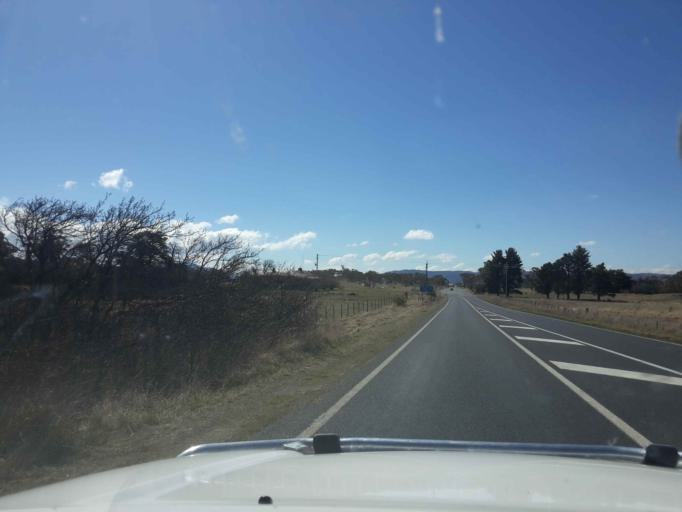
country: AU
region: New South Wales
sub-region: Snowy River
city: Jindabyne
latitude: -36.4350
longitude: 148.6073
